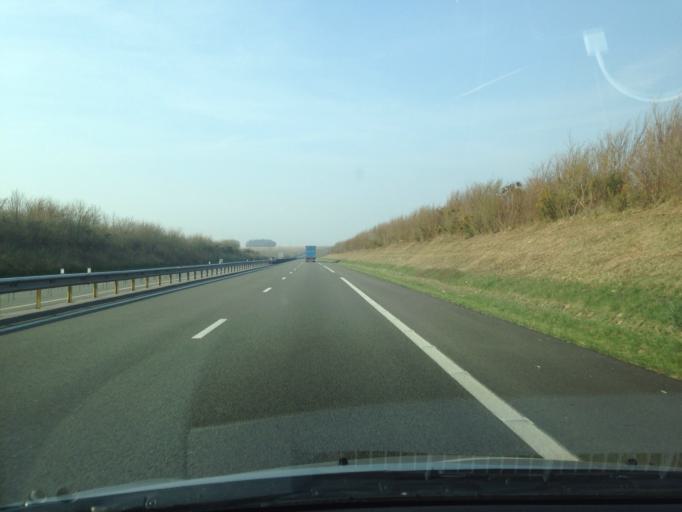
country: FR
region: Picardie
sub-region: Departement de la Somme
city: Sailly-Flibeaucourt
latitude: 50.2053
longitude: 1.7575
